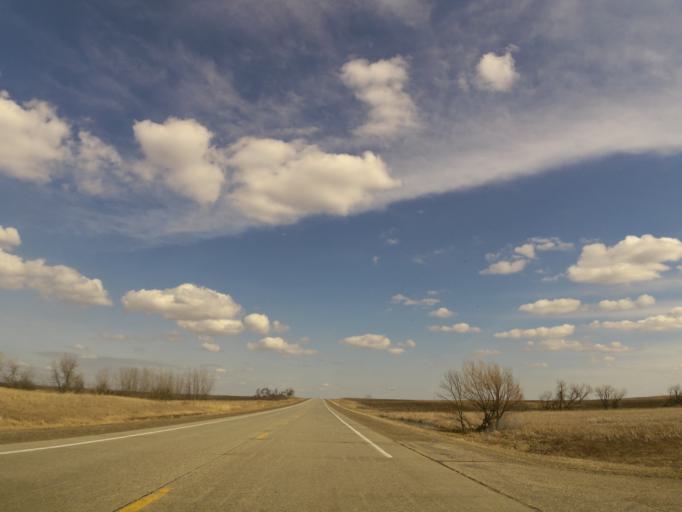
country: US
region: South Dakota
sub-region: Deuel County
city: Clear Lake
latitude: 44.8900
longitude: -96.7434
